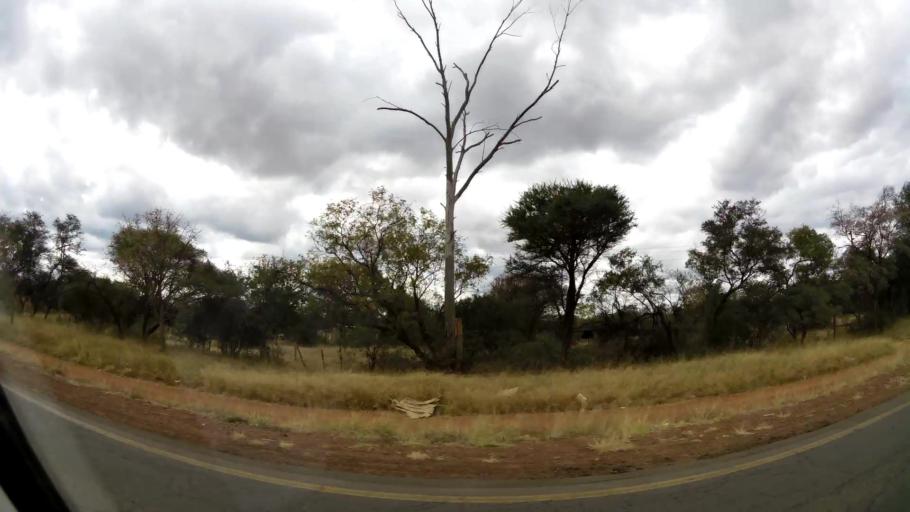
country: ZA
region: Limpopo
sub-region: Waterberg District Municipality
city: Modimolle
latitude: -24.7277
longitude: 28.4285
